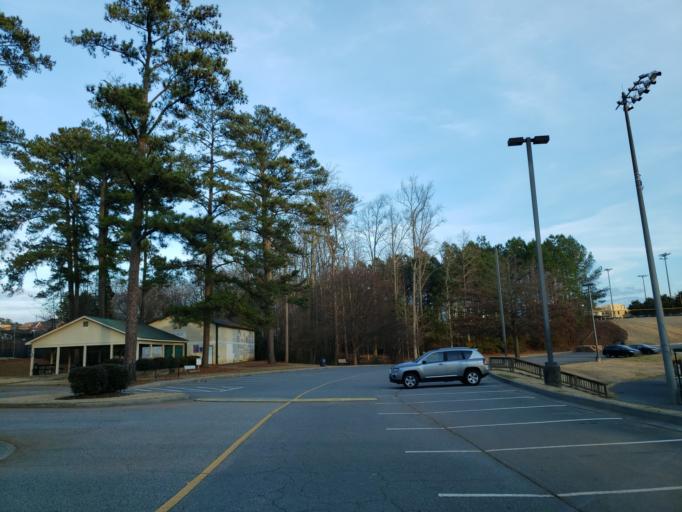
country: US
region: Georgia
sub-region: Cobb County
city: Kennesaw
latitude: 34.0242
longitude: -84.6217
